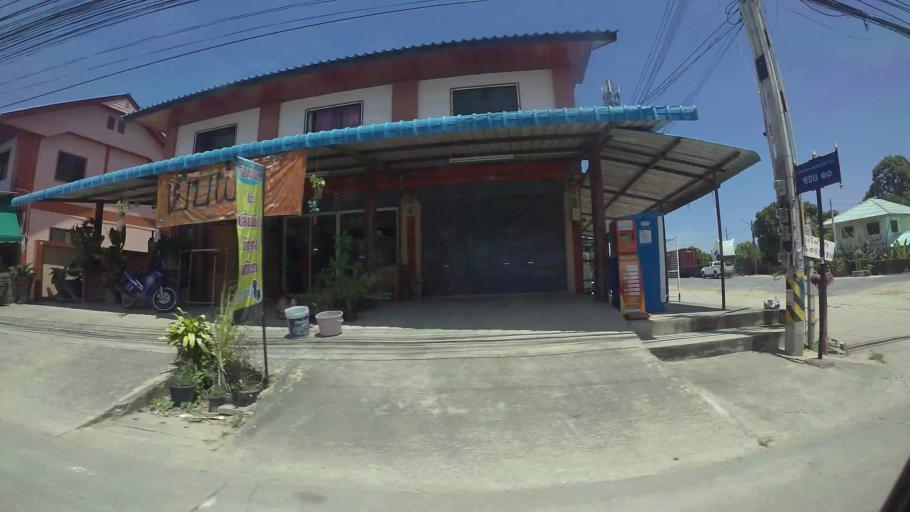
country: TH
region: Chon Buri
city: Si Racha
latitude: 13.1250
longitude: 100.9541
